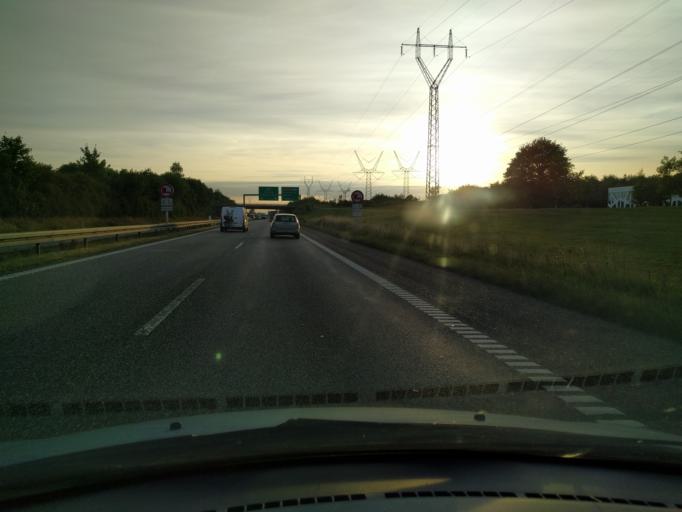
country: DK
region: South Denmark
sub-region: Odense Kommune
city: Neder Holluf
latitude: 55.3571
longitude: 10.4826
